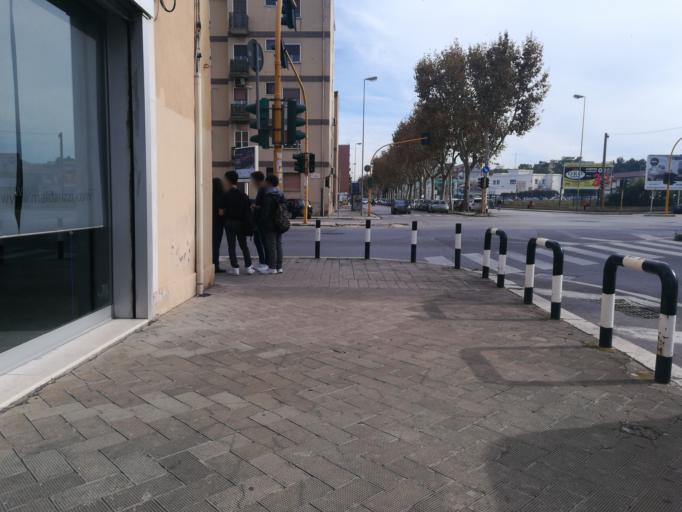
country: IT
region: Apulia
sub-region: Provincia di Bari
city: Bari
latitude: 41.1153
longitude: 16.8871
